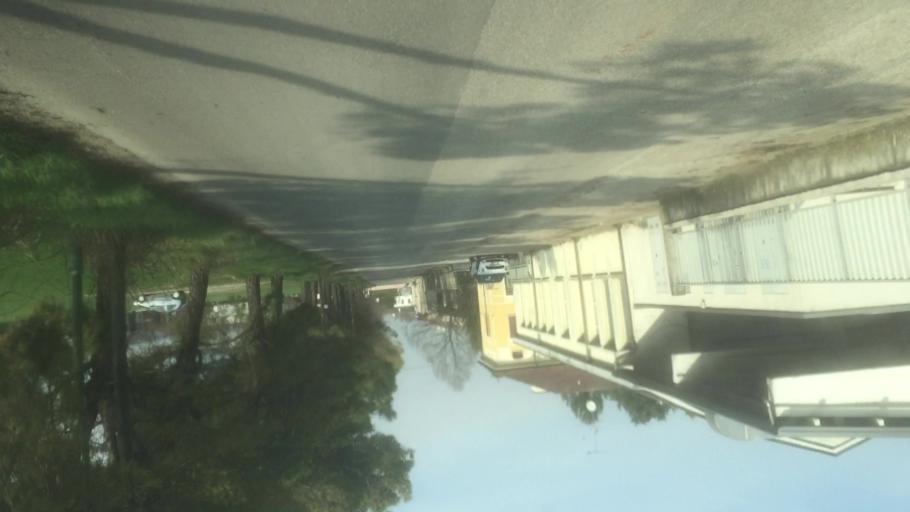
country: IT
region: Lombardy
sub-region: Provincia di Mantova
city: Cerlongo
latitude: 45.3006
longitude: 10.6397
